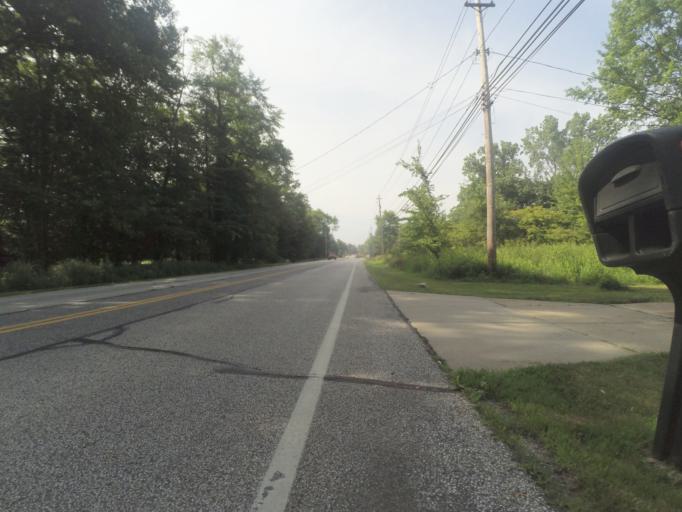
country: US
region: Ohio
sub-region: Cuyahoga County
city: Orange
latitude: 41.4509
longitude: -81.4803
